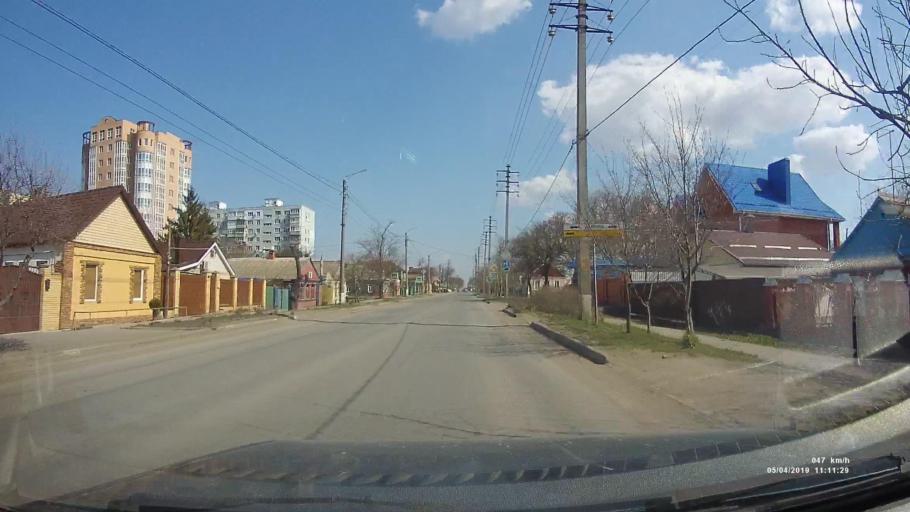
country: RU
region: Rostov
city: Azov
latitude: 47.0952
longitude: 39.4353
